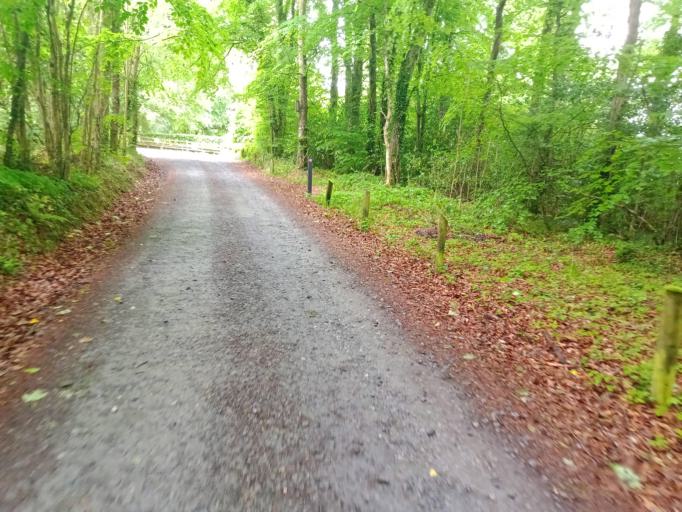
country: IE
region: Leinster
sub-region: Kilkenny
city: Thomastown
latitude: 52.4762
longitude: -7.0563
